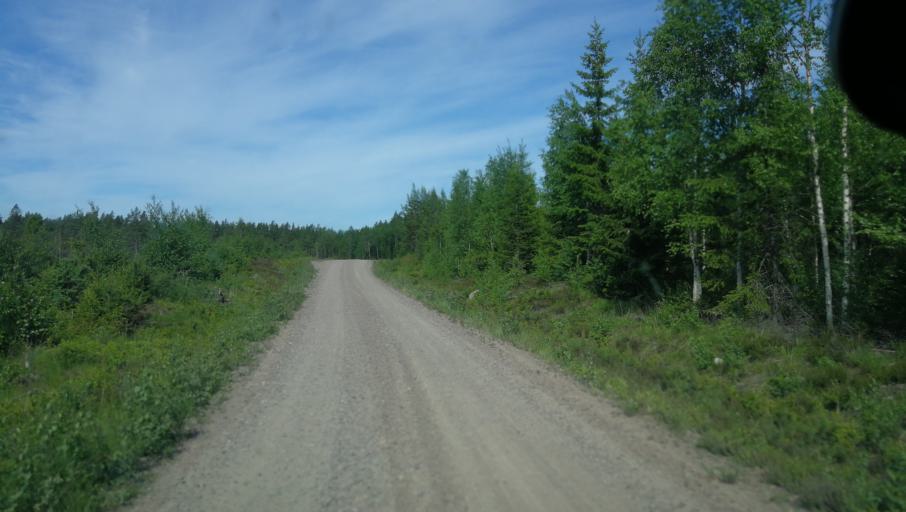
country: SE
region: Dalarna
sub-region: Vansbro Kommun
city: Vansbro
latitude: 60.8208
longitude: 14.1725
